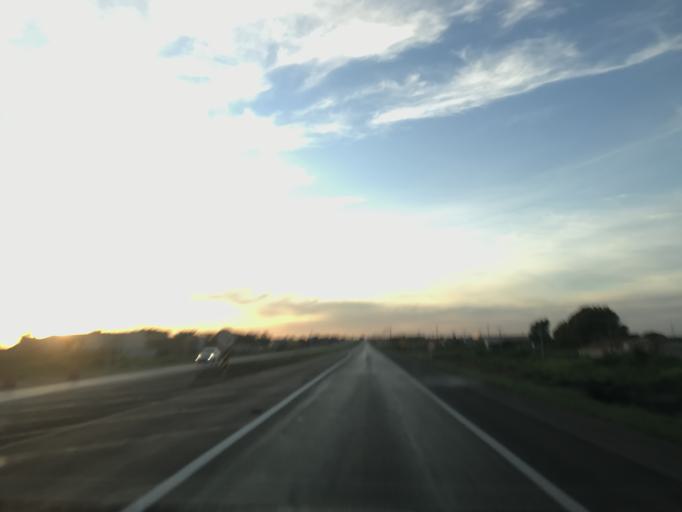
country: BR
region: Goias
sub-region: Luziania
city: Luziania
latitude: -16.2517
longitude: -47.9014
